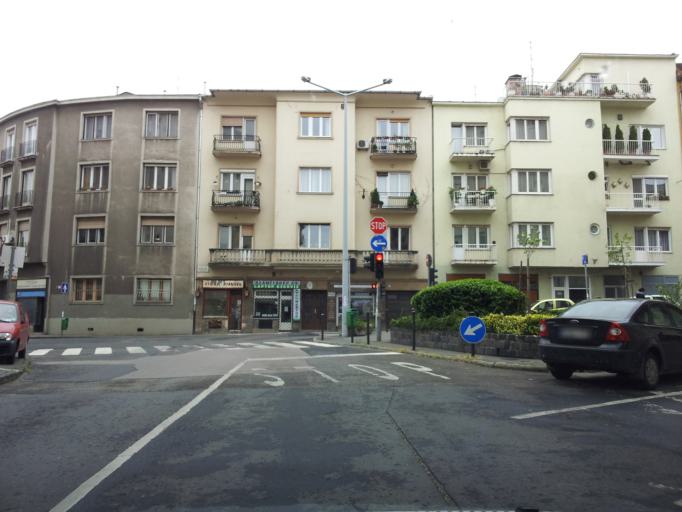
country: HU
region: Budapest
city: Budapest II. keruelet
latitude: 47.5072
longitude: 19.0342
